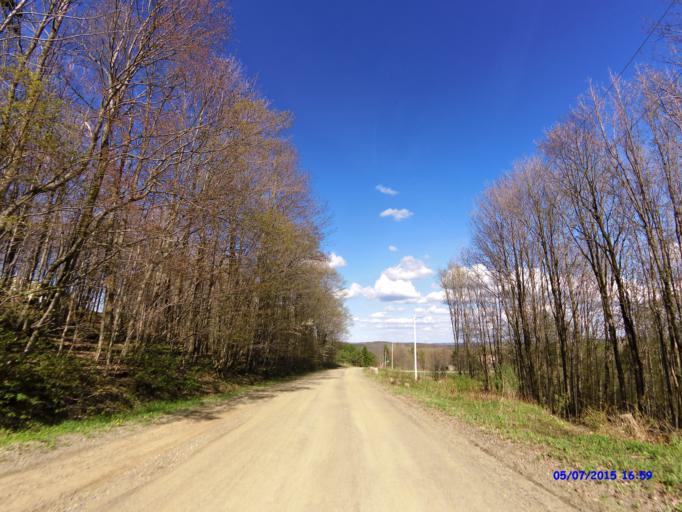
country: US
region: New York
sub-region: Cattaraugus County
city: Little Valley
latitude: 42.2892
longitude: -78.7345
